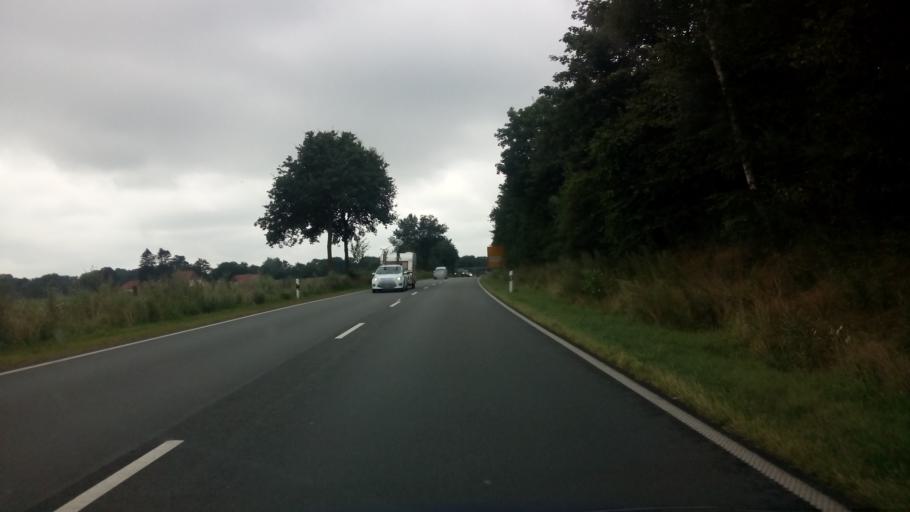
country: DE
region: Lower Saxony
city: Bassum
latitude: 52.8520
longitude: 8.7525
